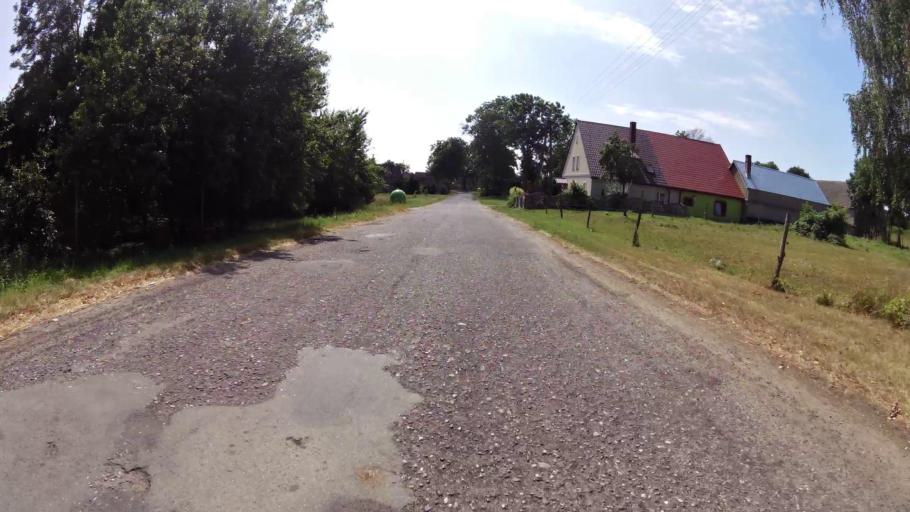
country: PL
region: West Pomeranian Voivodeship
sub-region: Powiat stargardzki
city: Suchan
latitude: 53.2702
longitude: 15.4081
